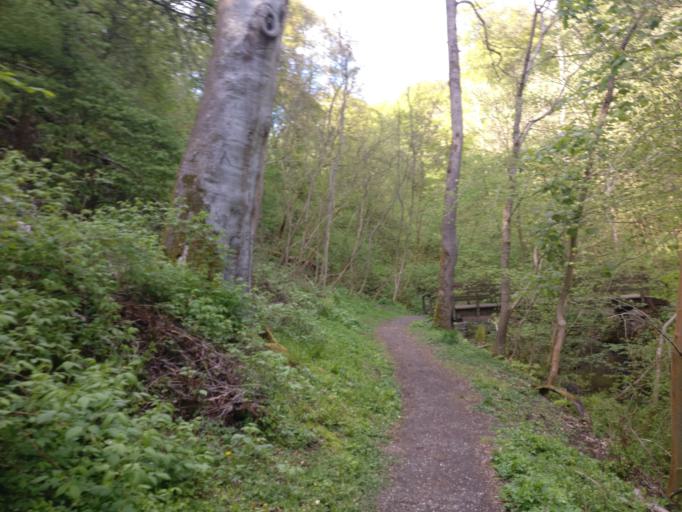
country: GB
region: Scotland
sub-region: Fife
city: Lundin Links
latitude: 56.2249
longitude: -2.9457
